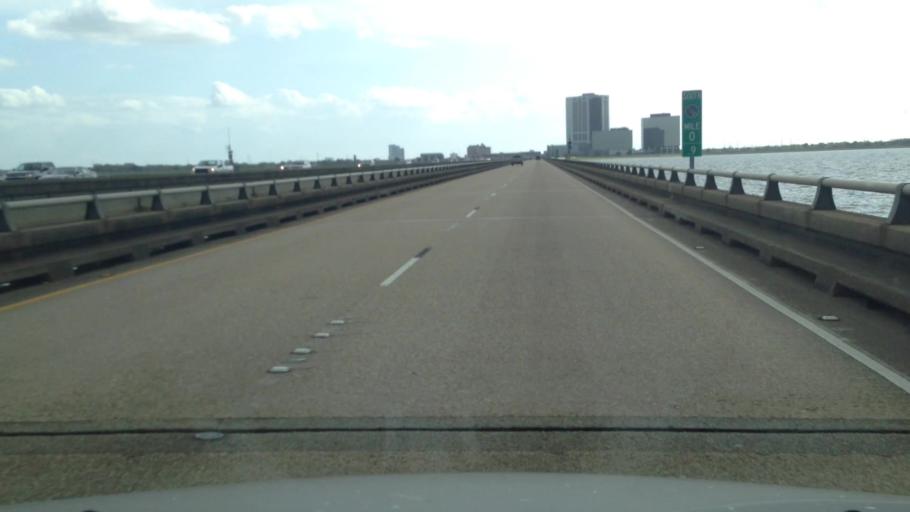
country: US
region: Louisiana
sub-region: Jefferson Parish
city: Metairie
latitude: 30.0348
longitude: -90.1519
